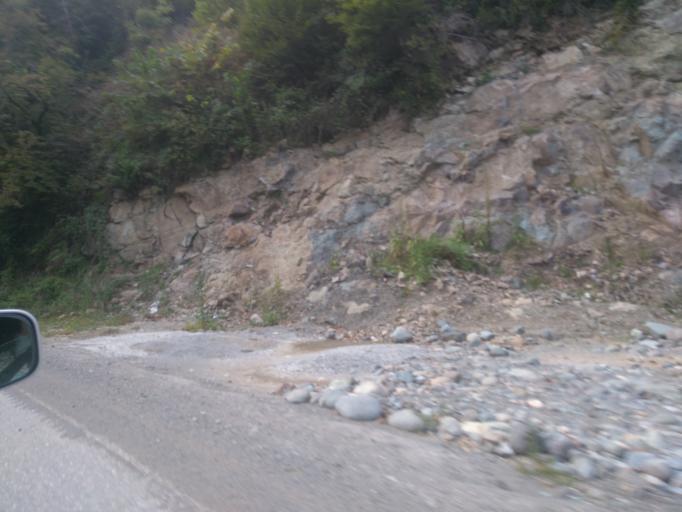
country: TR
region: Artvin
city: Muratli
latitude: 41.5474
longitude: 41.7399
